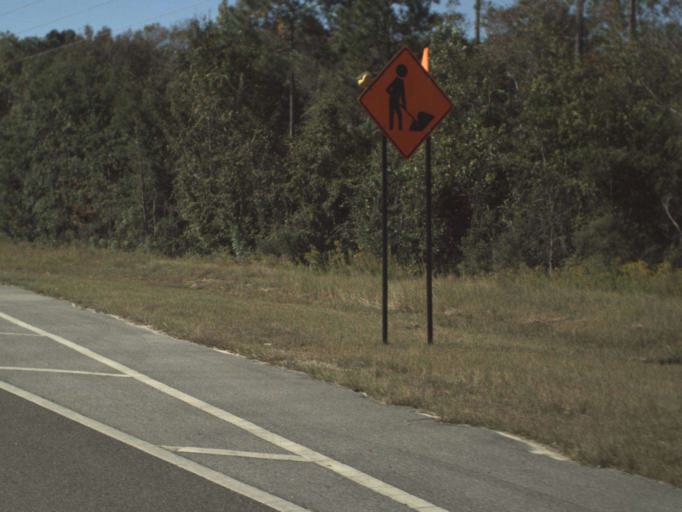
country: US
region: Florida
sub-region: Walton County
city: Freeport
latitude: 30.4941
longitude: -86.1202
